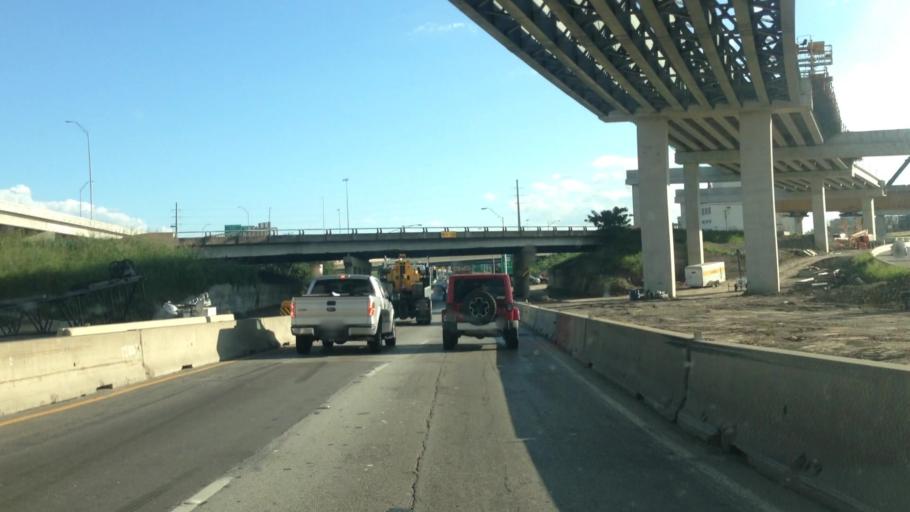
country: US
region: Texas
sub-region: Tarrant County
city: Fort Worth
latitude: 32.7662
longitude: -97.3187
